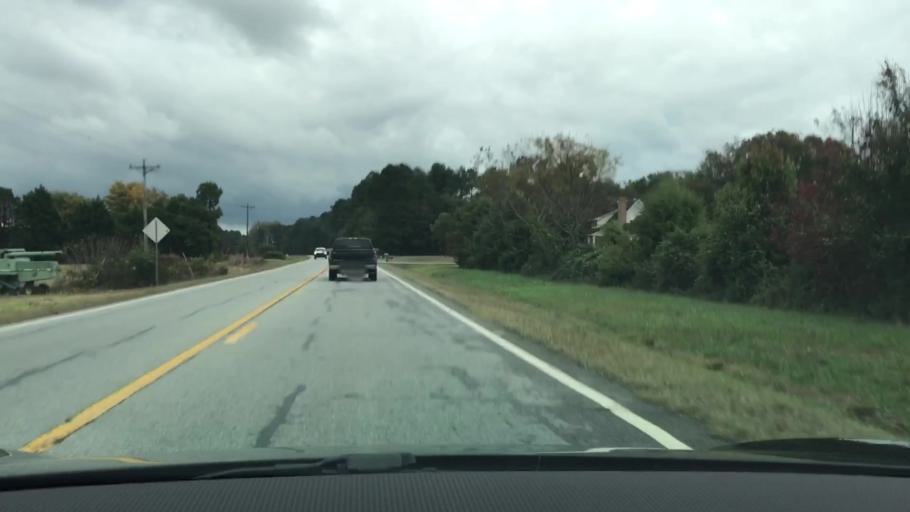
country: US
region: Georgia
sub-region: Oconee County
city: Watkinsville
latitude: 33.8163
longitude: -83.3625
